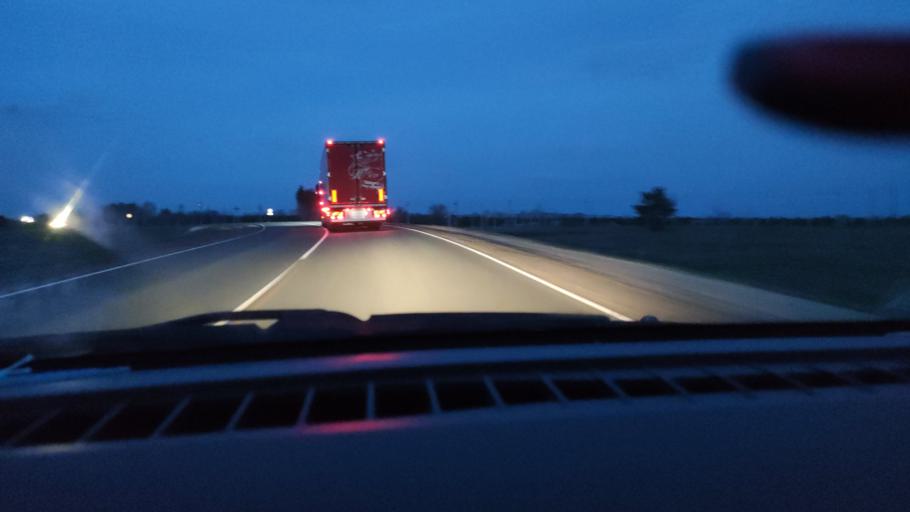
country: RU
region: Saratov
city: Sennoy
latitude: 52.1426
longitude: 46.9188
